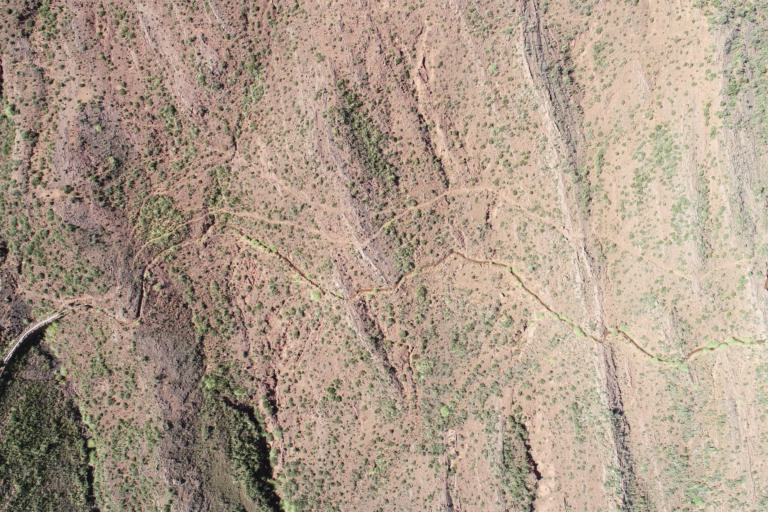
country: BO
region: La Paz
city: Tiahuanaco
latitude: -16.6057
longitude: -68.7576
